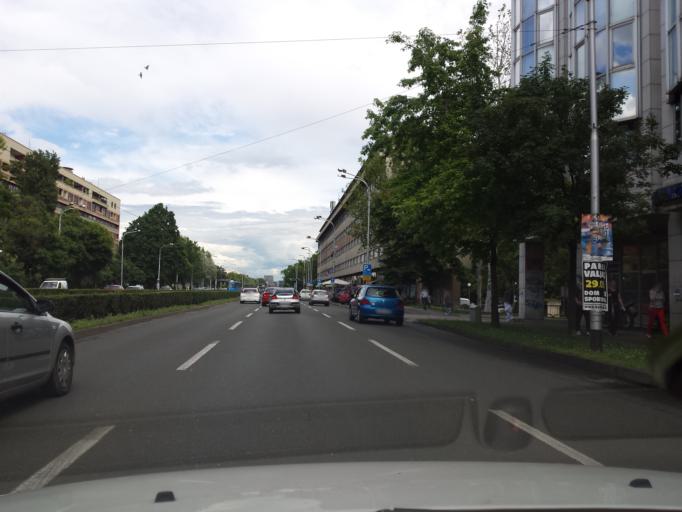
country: HR
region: Grad Zagreb
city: Zagreb - Centar
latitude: 45.7995
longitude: 15.9648
